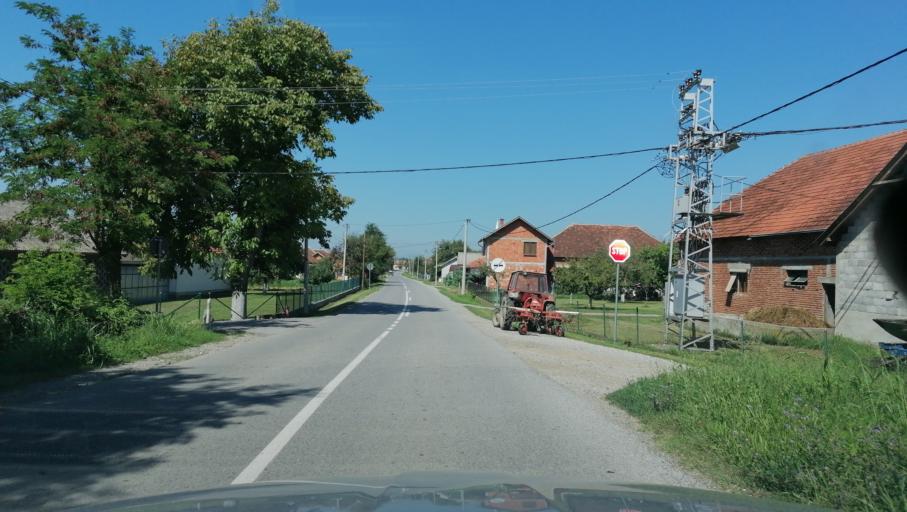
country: RS
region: Central Serbia
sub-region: Raski Okrug
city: Vrnjacka Banja
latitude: 43.6871
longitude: 20.8756
